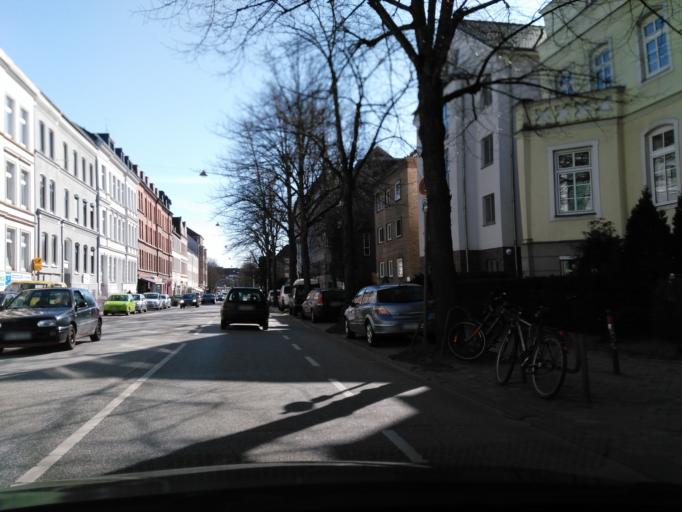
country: DE
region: Schleswig-Holstein
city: Kiel
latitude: 54.3257
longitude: 10.1277
